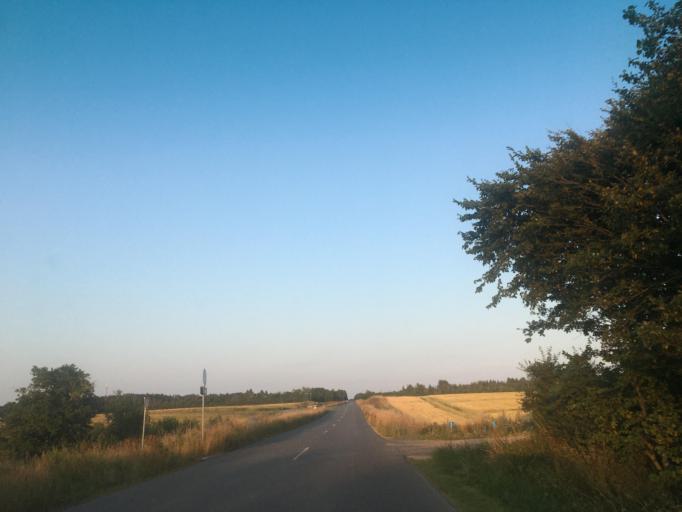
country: DK
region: North Denmark
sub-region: Thisted Kommune
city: Hurup
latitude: 56.7551
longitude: 8.3695
